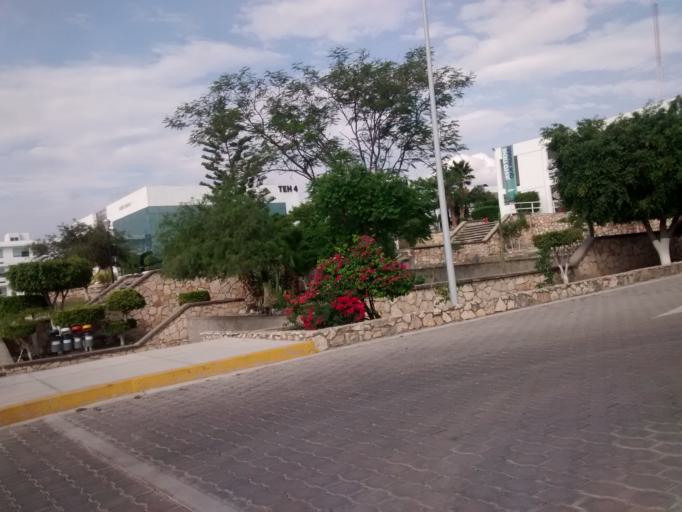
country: MX
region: Puebla
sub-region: Tehuacan
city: Santa Cruz Acapa
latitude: 18.4176
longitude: -97.3642
